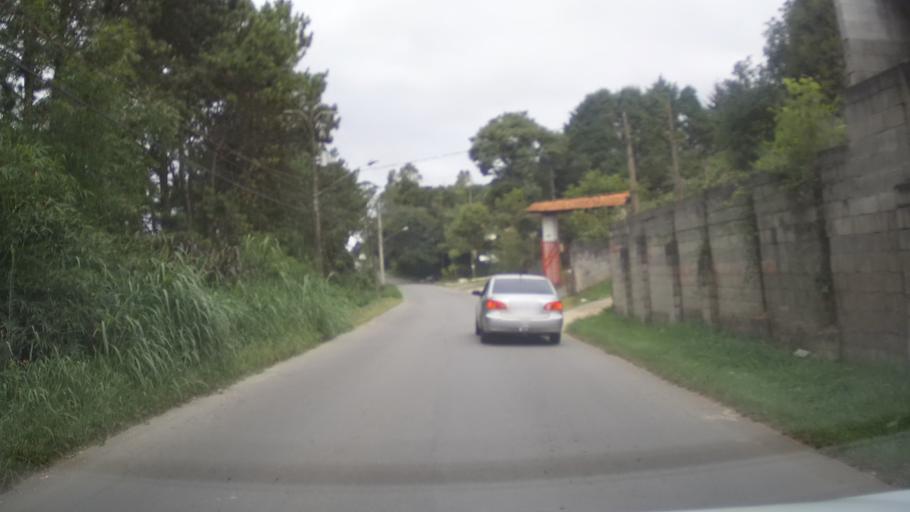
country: BR
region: Sao Paulo
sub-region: Aruja
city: Aruja
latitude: -23.3744
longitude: -46.3006
